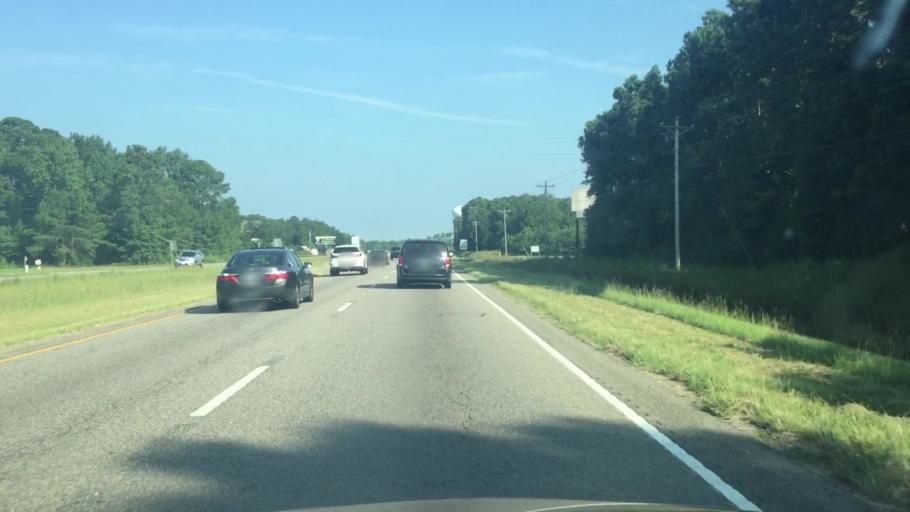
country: US
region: South Carolina
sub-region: Horry County
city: North Myrtle Beach
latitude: 33.8945
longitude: -78.6940
